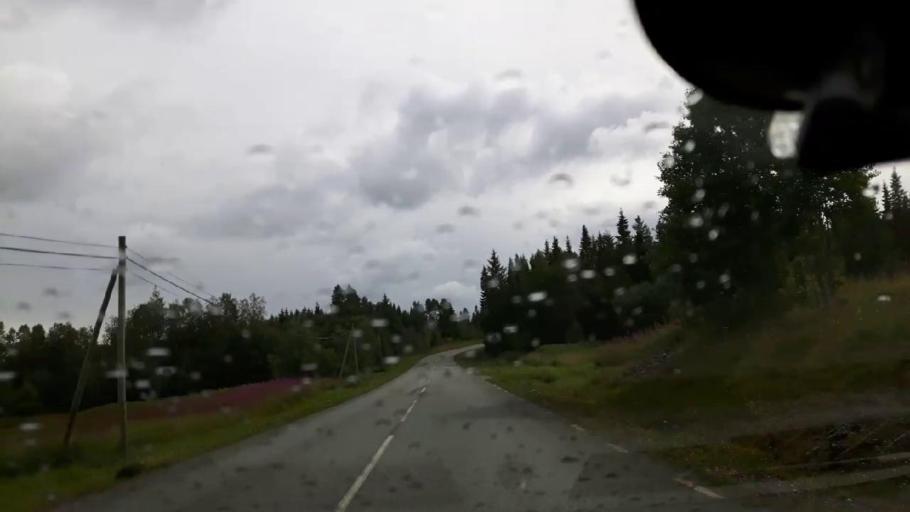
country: SE
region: Jaemtland
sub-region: Krokoms Kommun
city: Valla
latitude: 63.3961
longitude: 13.8189
